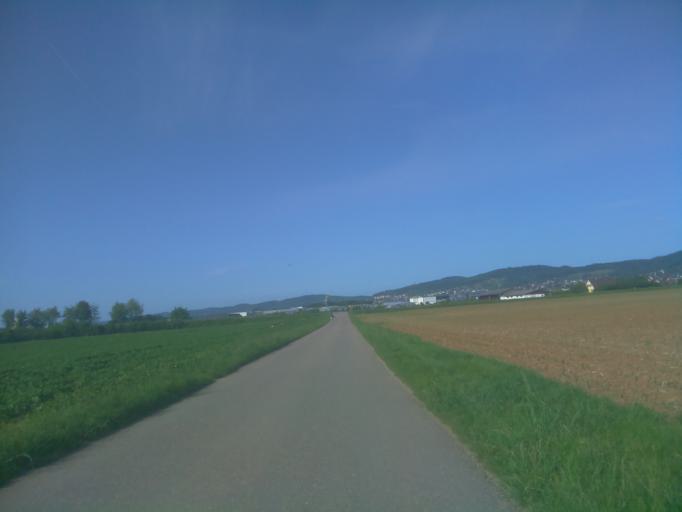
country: DE
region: Baden-Wuerttemberg
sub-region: Karlsruhe Region
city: Heddesheim
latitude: 49.4995
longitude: 8.6283
